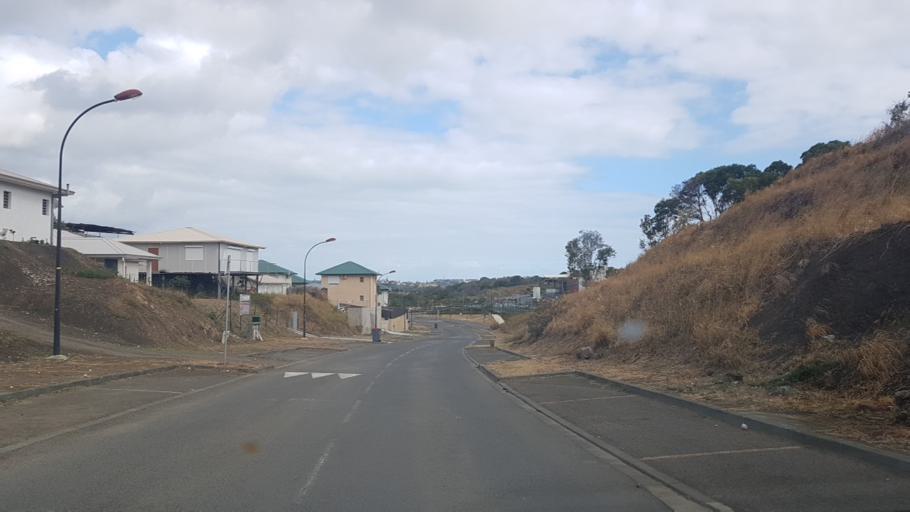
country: NC
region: South Province
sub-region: Dumbea
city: Dumbea
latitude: -22.2038
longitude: 166.4440
